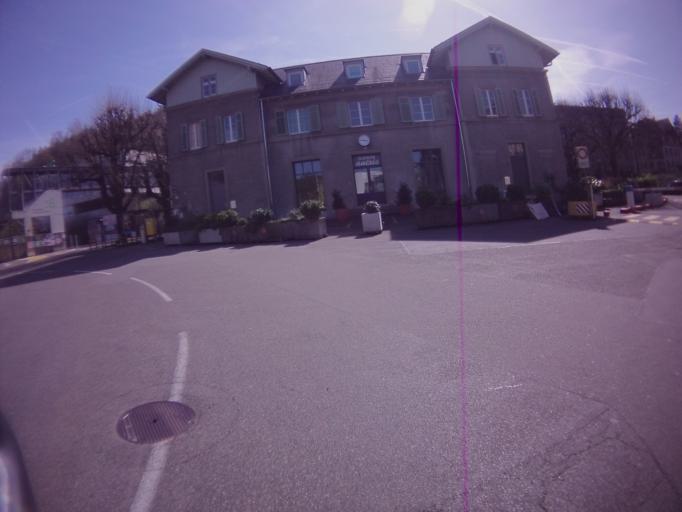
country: CH
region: Aargau
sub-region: Bezirk Baden
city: Baden
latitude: 47.4701
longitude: 8.3045
